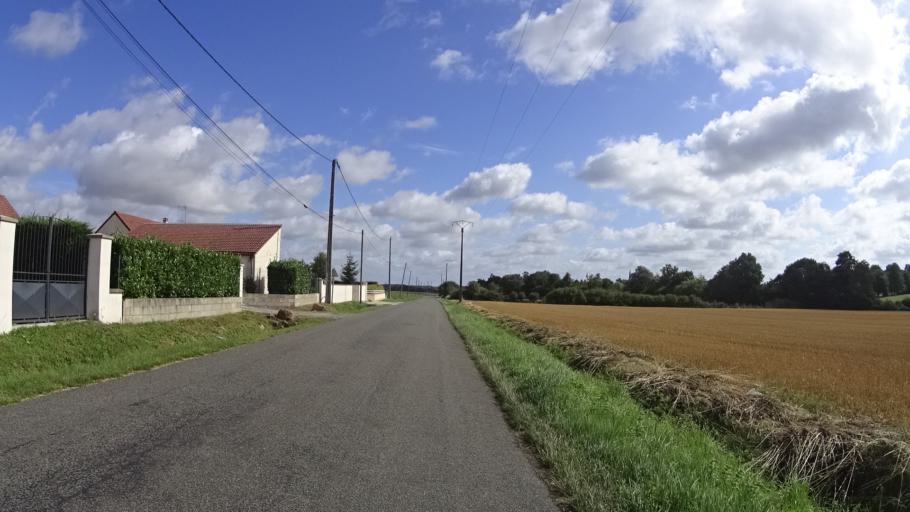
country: FR
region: Centre
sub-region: Departement du Loiret
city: Lorris
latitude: 47.9107
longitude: 2.5175
